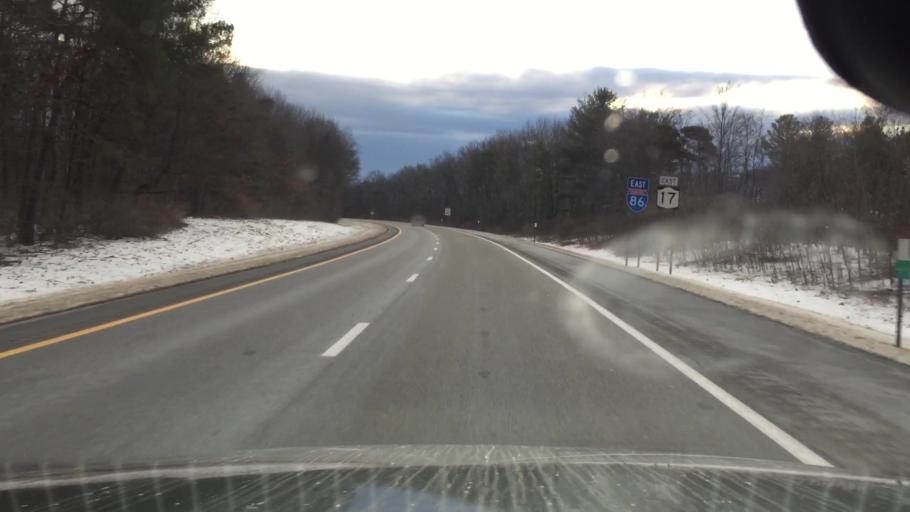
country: US
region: Pennsylvania
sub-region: Bradford County
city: South Waverly
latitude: 42.0014
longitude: -76.6195
